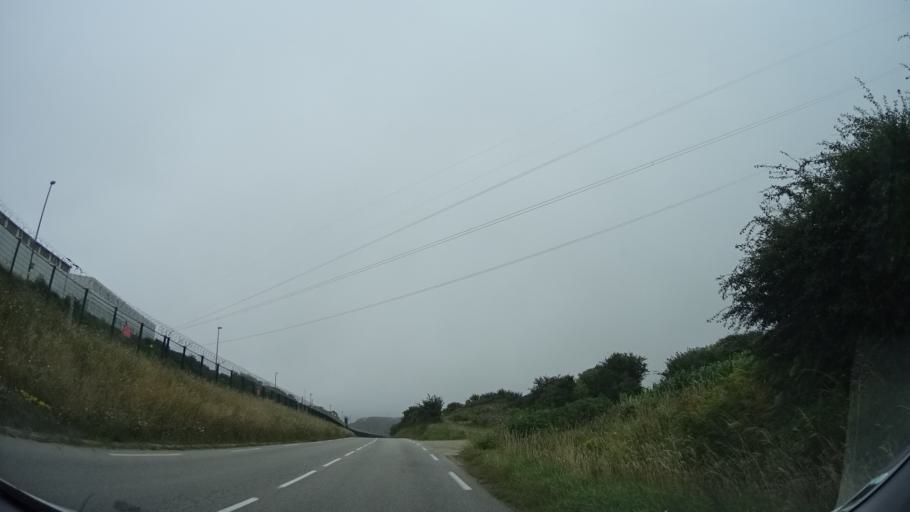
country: FR
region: Lower Normandy
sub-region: Departement de la Manche
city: Flamanville
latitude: 49.5372
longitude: -1.8758
